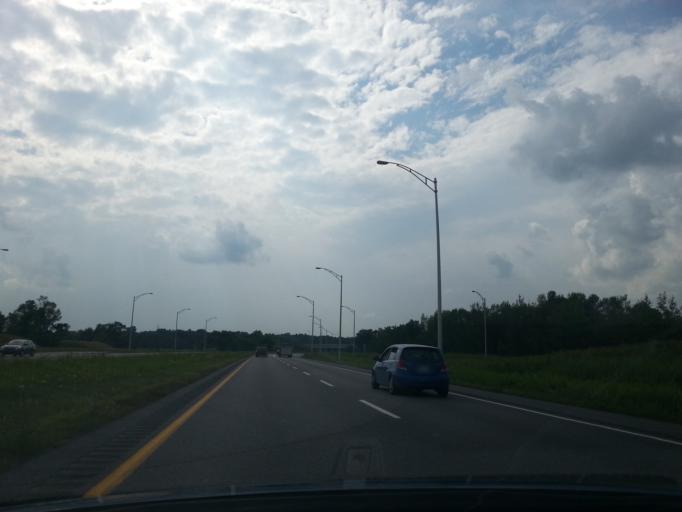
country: CA
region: Quebec
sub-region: Monteregie
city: Saint-Lazare
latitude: 45.4255
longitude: -74.1133
